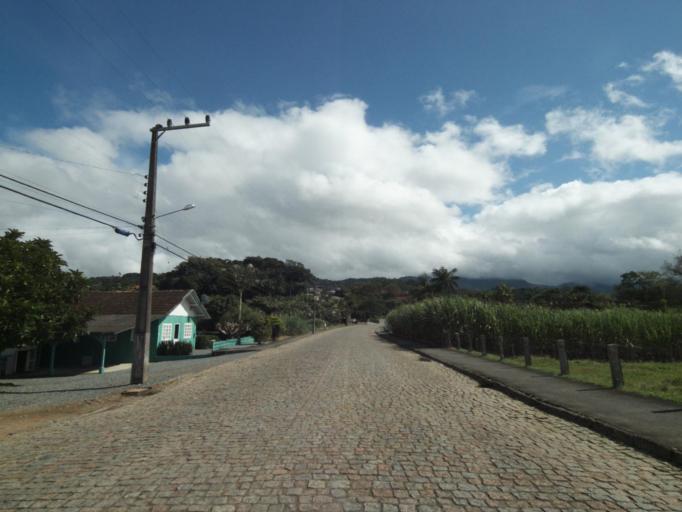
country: BR
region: Santa Catarina
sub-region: Pomerode
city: Pomerode
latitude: -26.7025
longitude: -49.1706
